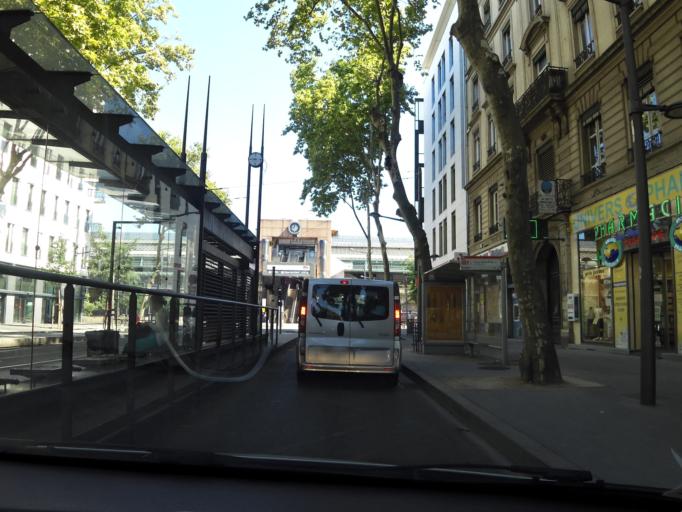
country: FR
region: Rhone-Alpes
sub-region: Departement du Rhone
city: Lyon
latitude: 45.7470
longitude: 4.8247
